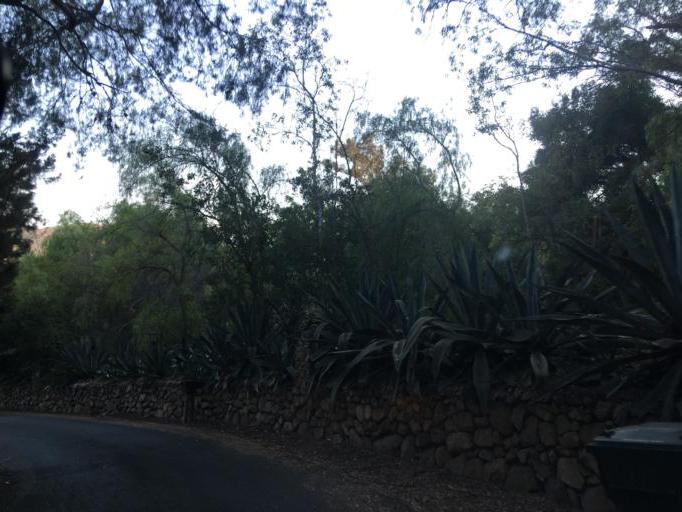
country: US
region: California
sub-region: Los Angeles County
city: Malibu Beach
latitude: 34.0801
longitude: -118.6849
